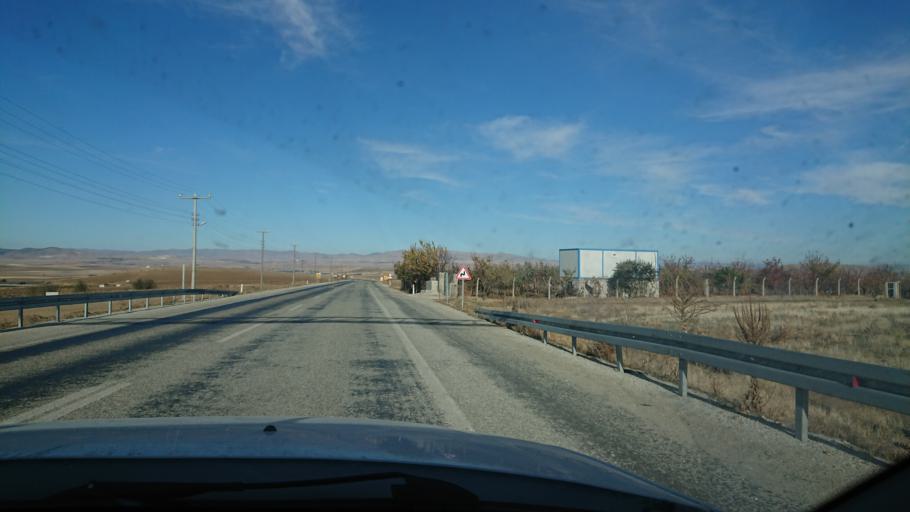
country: TR
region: Aksaray
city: Sariyahsi
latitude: 38.9941
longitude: 33.8491
